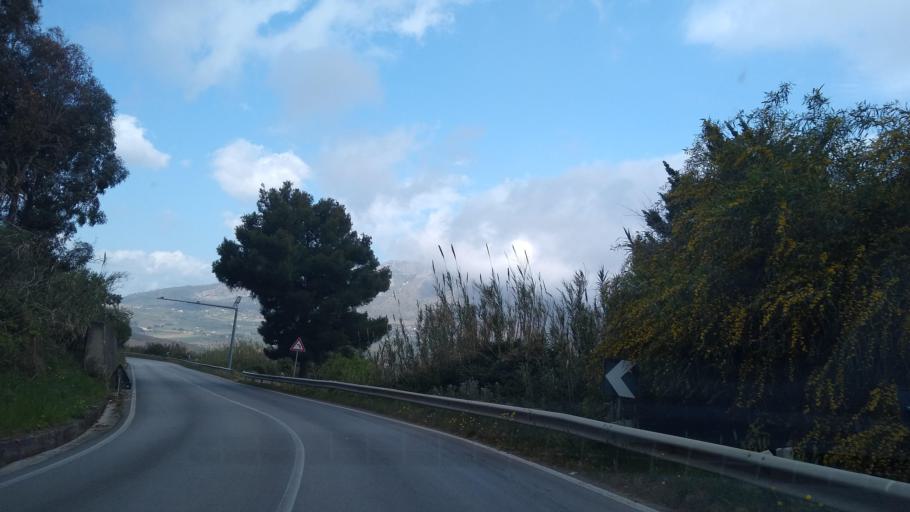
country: IT
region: Sicily
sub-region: Trapani
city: Alcamo
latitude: 37.9788
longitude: 12.9381
